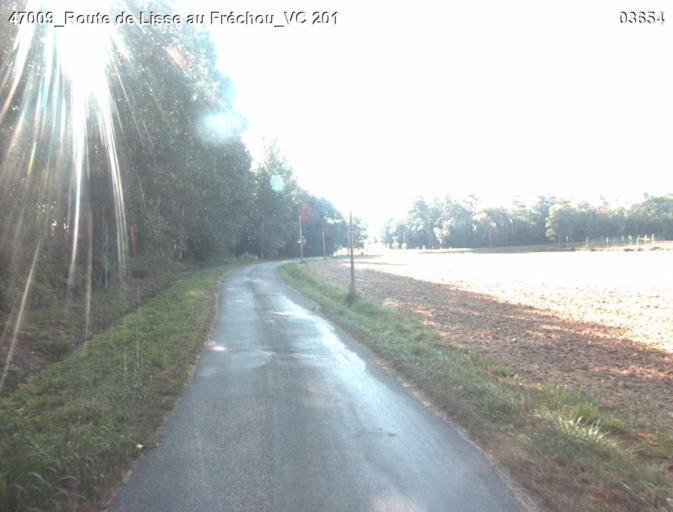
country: FR
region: Aquitaine
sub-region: Departement du Lot-et-Garonne
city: Mezin
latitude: 44.1016
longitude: 0.2750
